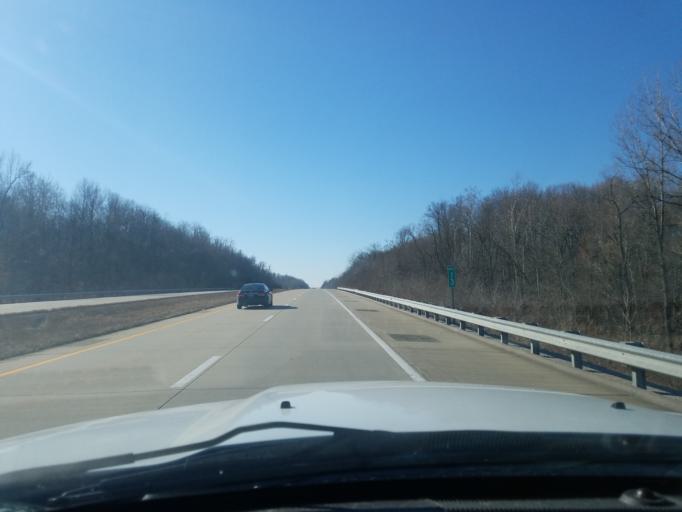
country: US
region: Indiana
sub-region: Warrick County
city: Newburgh
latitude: 37.7573
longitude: -87.3450
